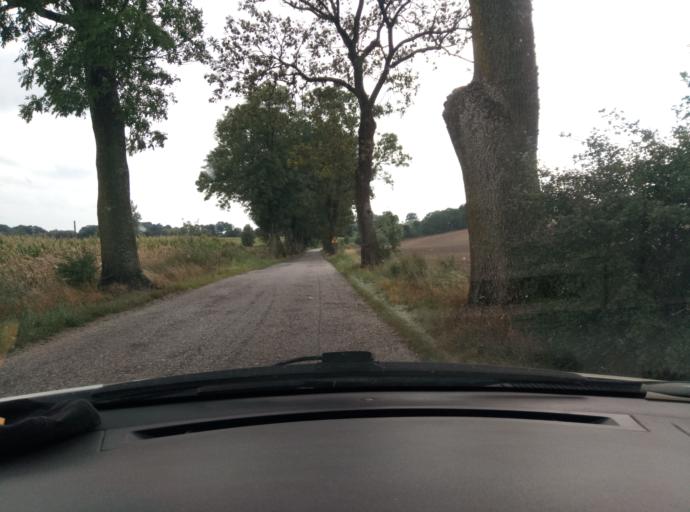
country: PL
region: Warmian-Masurian Voivodeship
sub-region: Powiat nowomiejski
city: Biskupiec
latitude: 53.4350
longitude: 19.2773
